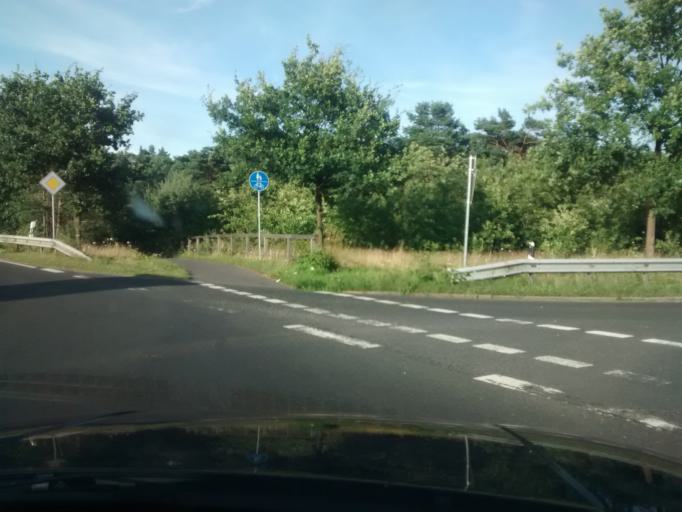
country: DE
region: Lower Saxony
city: Meppen
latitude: 52.7116
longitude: 7.2959
